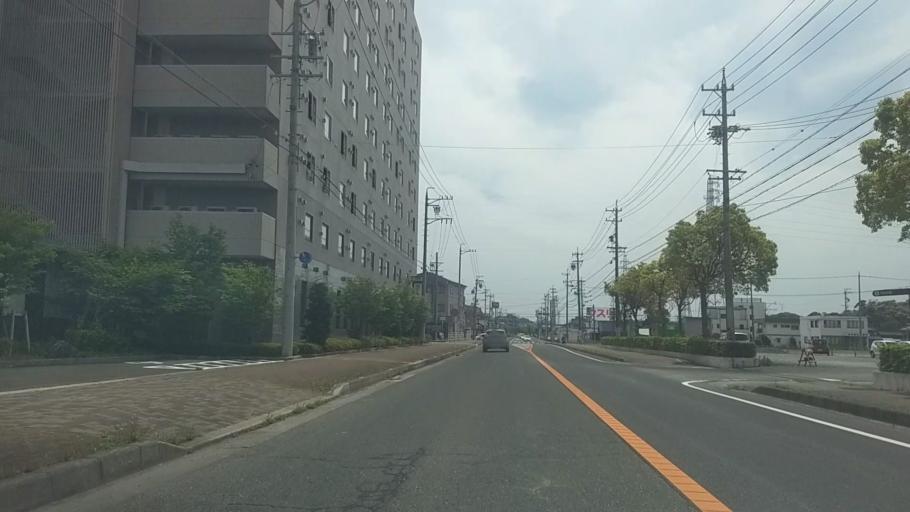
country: JP
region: Shizuoka
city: Kosai-shi
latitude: 34.7196
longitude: 137.5325
